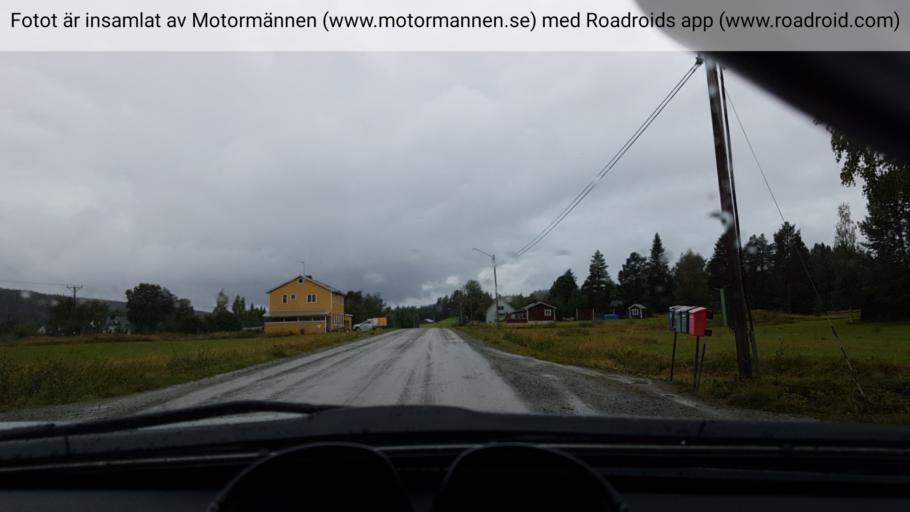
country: SE
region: Vaesterbotten
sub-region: Lycksele Kommun
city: Soderfors
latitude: 64.9668
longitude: 17.6122
